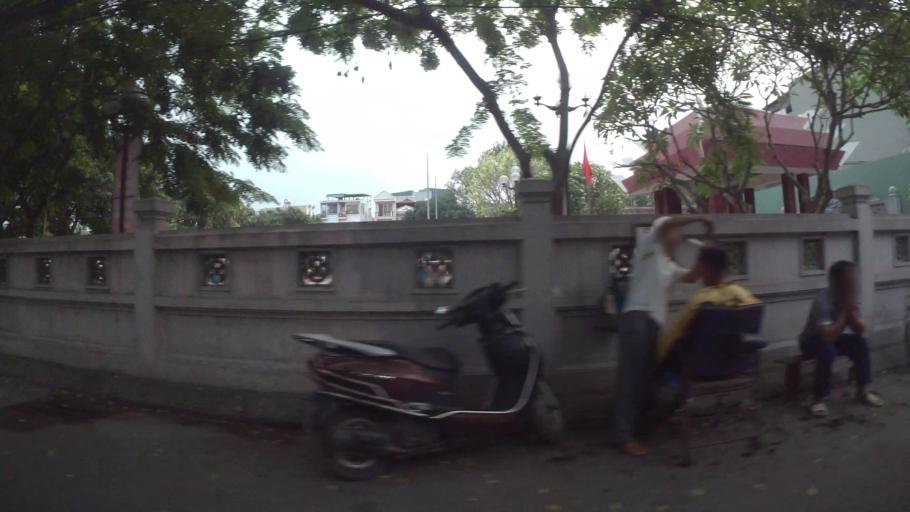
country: VN
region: Ha Noi
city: Hoan Kiem
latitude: 21.0573
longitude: 105.8954
